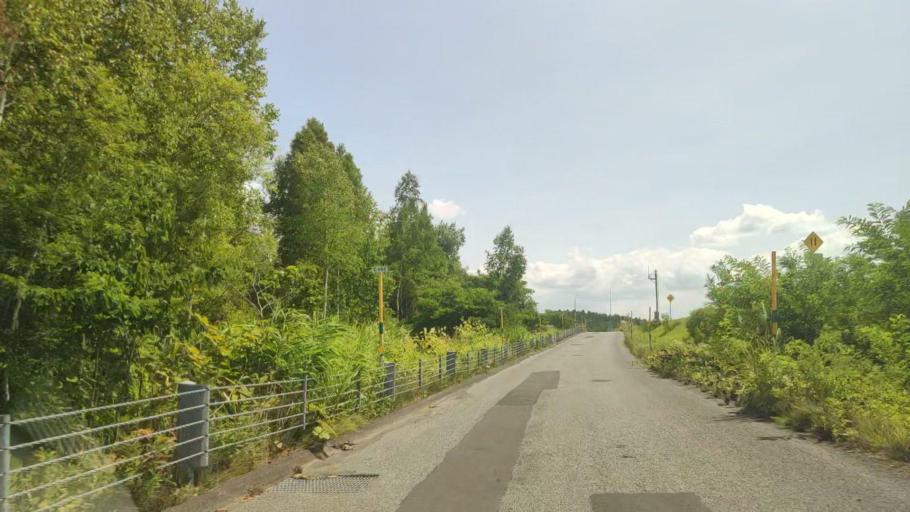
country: JP
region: Hokkaido
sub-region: Asahikawa-shi
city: Asahikawa
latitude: 43.9196
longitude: 142.4992
